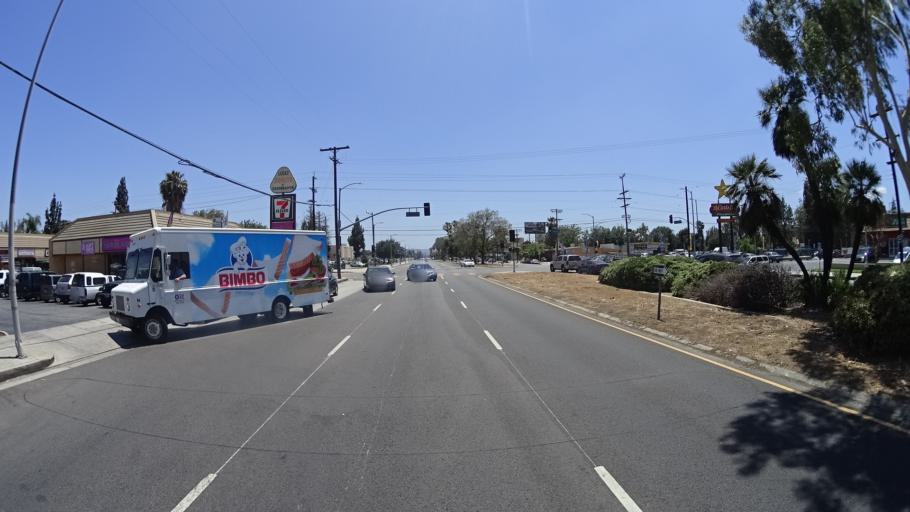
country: US
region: California
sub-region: Los Angeles County
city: San Fernando
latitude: 34.2433
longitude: -118.4674
